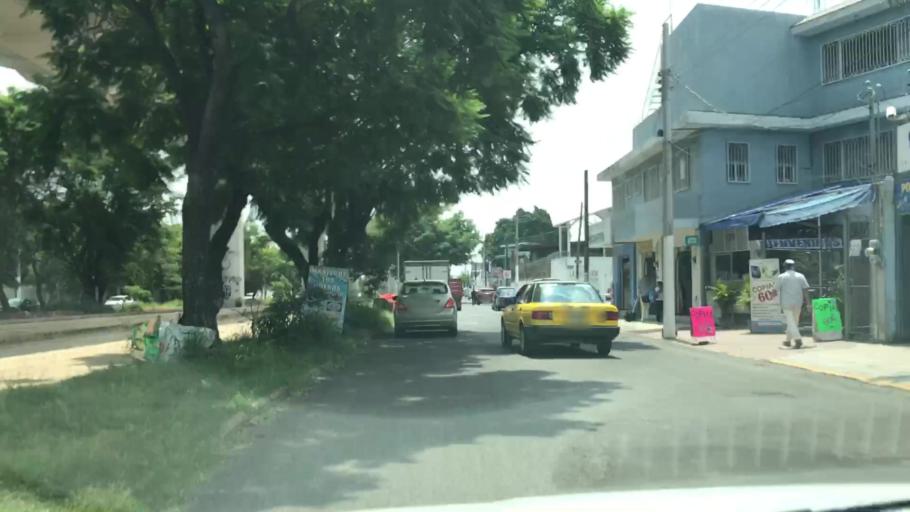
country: MX
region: Jalisco
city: Zapopan2
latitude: 20.7360
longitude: -103.4004
